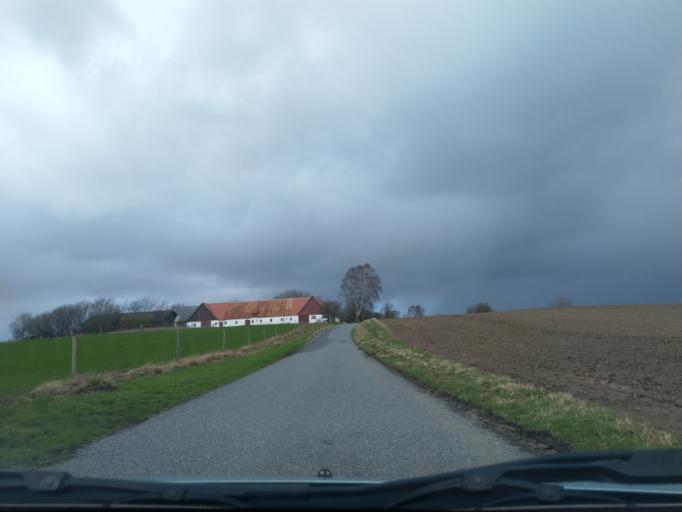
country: DK
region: Zealand
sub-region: Naestved Kommune
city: Fuglebjerg
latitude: 55.3441
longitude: 11.5840
